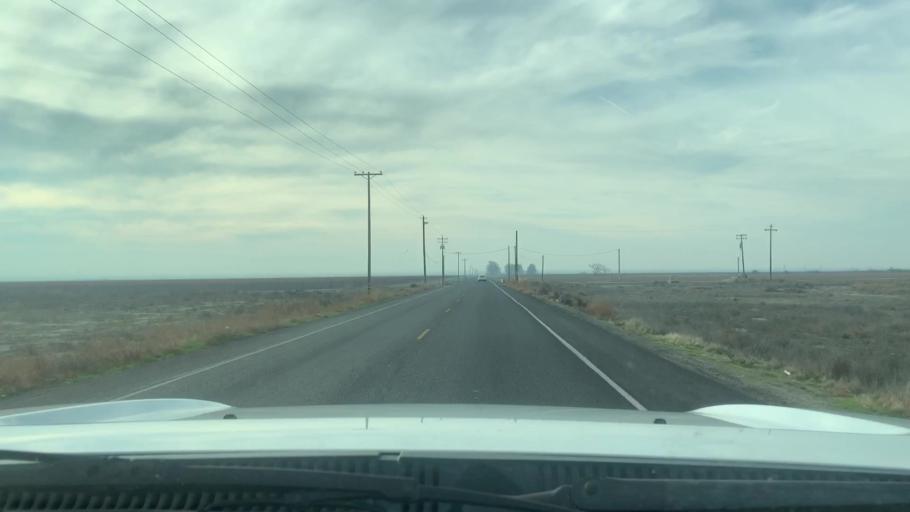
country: US
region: California
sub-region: Kern County
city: Buttonwillow
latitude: 35.4997
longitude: -119.5651
